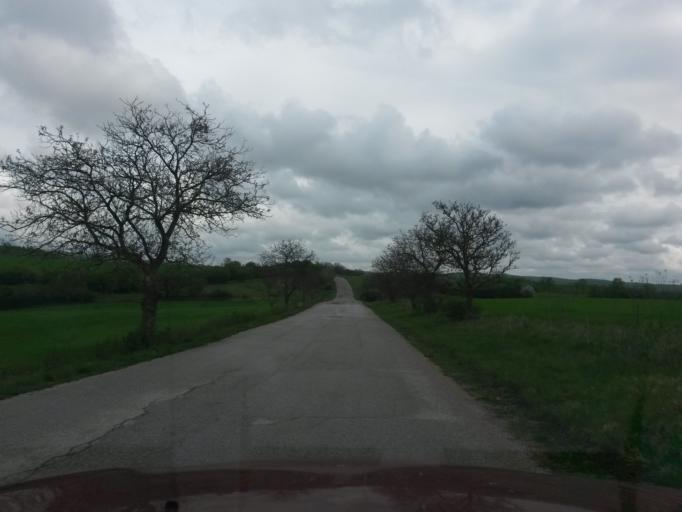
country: SK
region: Kosicky
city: Roznava
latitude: 48.5595
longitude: 20.4980
